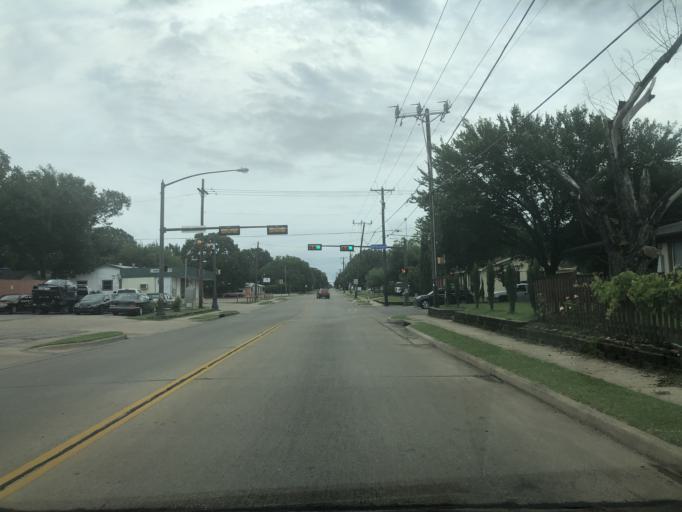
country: US
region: Texas
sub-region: Dallas County
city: Irving
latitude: 32.8086
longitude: -96.9475
